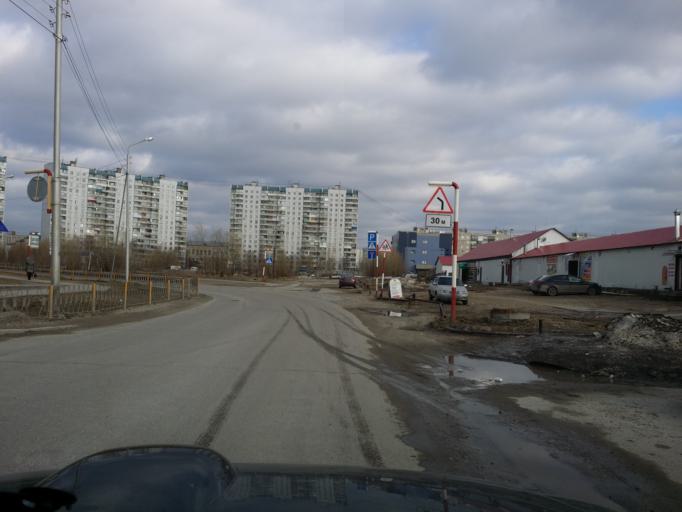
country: RU
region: Khanty-Mansiyskiy Avtonomnyy Okrug
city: Nizhnevartovsk
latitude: 60.9390
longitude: 76.6029
